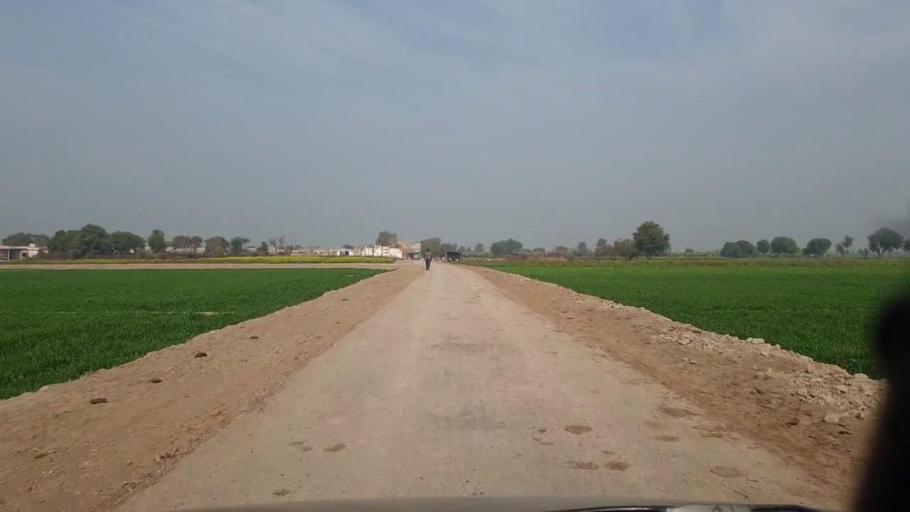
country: PK
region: Sindh
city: Shahdadpur
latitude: 26.0112
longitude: 68.5102
